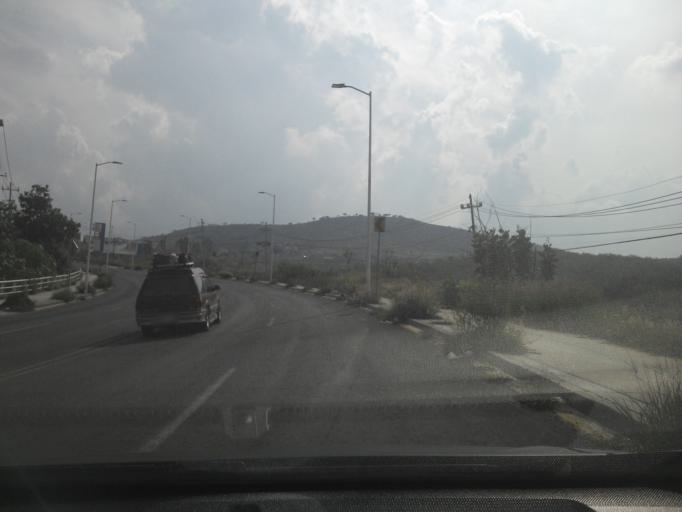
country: MX
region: Jalisco
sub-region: Tlajomulco de Zuniga
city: Lomas del Sur
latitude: 20.4953
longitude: -103.4184
